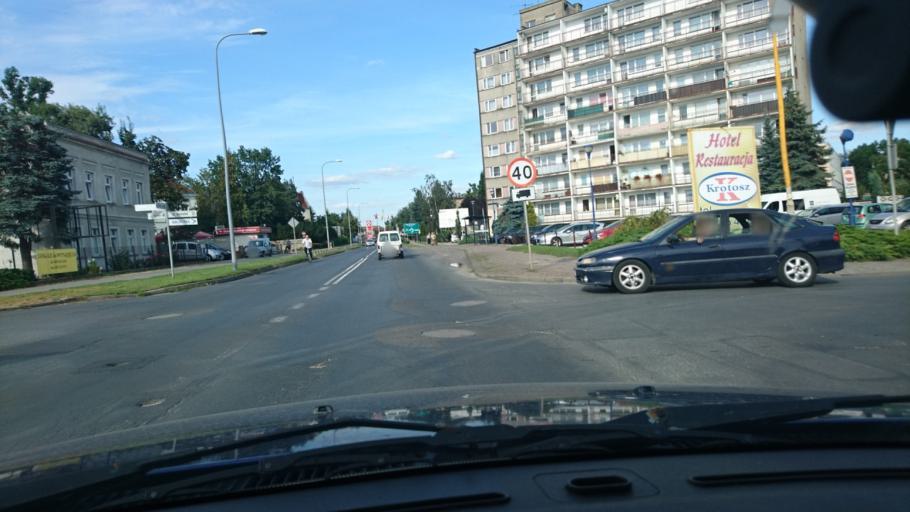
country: PL
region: Greater Poland Voivodeship
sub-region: Powiat krotoszynski
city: Krotoszyn
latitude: 51.6998
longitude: 17.4362
